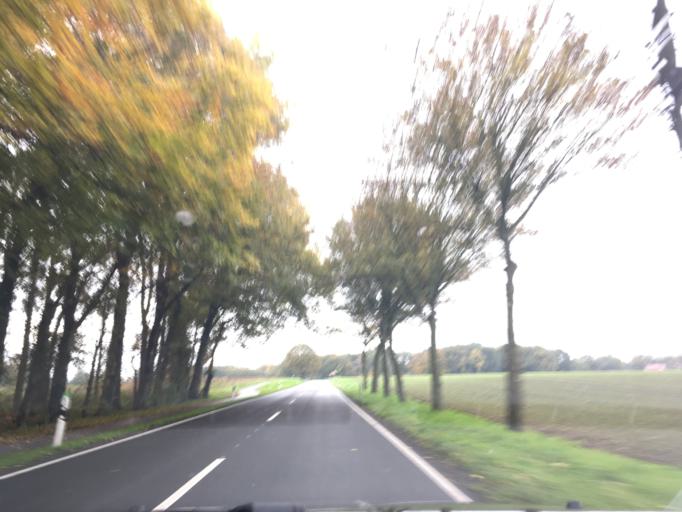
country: DE
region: North Rhine-Westphalia
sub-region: Regierungsbezirk Munster
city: Vreden
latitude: 52.0590
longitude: 6.7654
